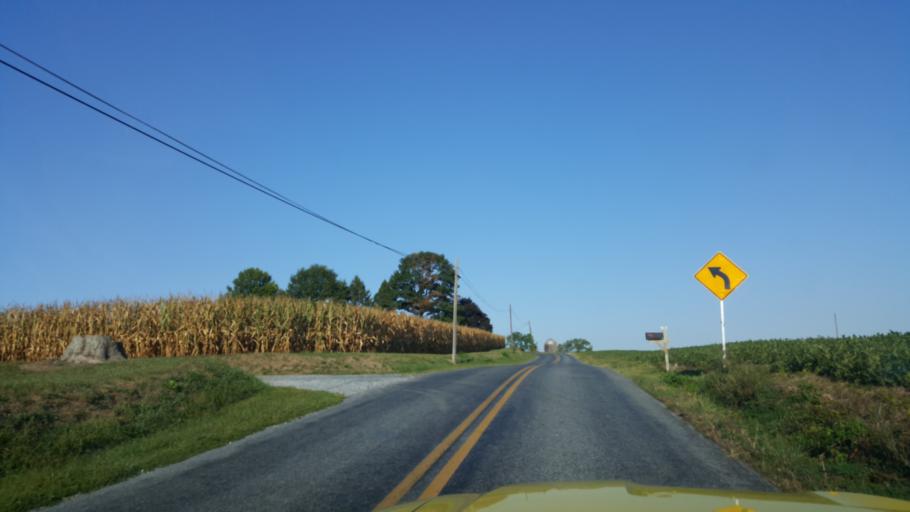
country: US
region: Pennsylvania
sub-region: Lancaster County
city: Rheems
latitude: 40.1591
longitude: -76.5480
